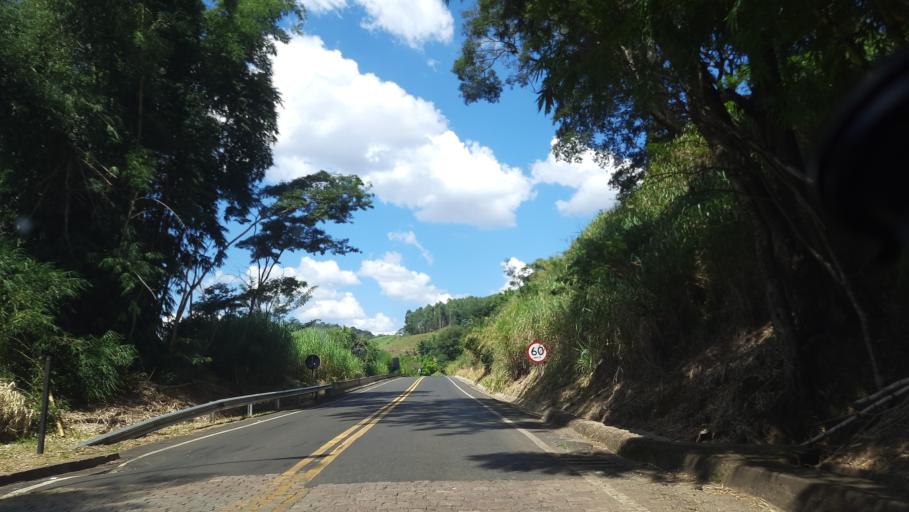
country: BR
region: Sao Paulo
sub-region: Sao Jose Do Rio Pardo
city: Sao Jose do Rio Pardo
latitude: -21.6045
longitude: -46.9469
